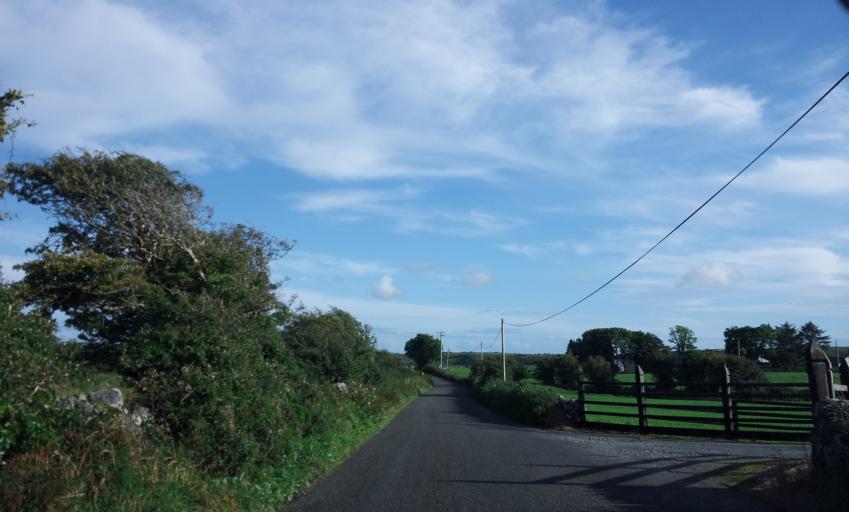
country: IE
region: Connaught
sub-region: County Galway
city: Bearna
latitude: 53.0449
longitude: -9.1391
